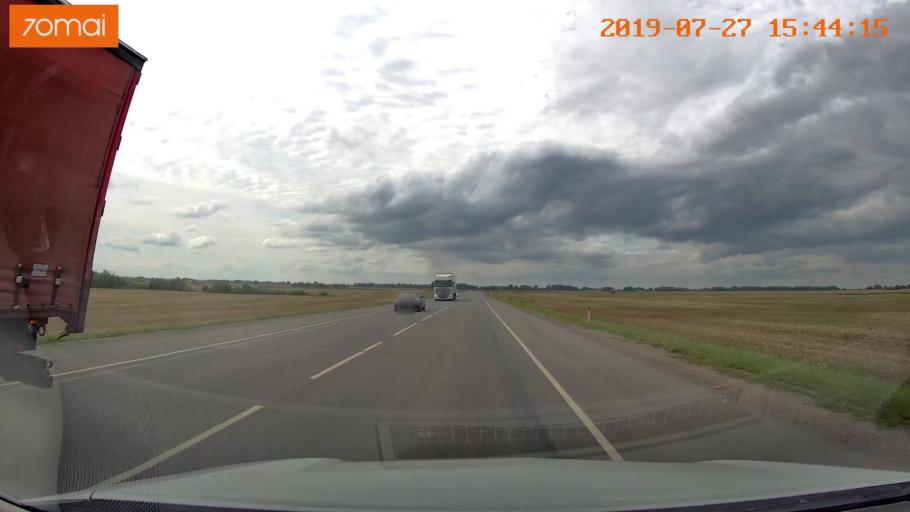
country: RU
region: Kaliningrad
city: Gusev
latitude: 54.6146
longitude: 22.1702
